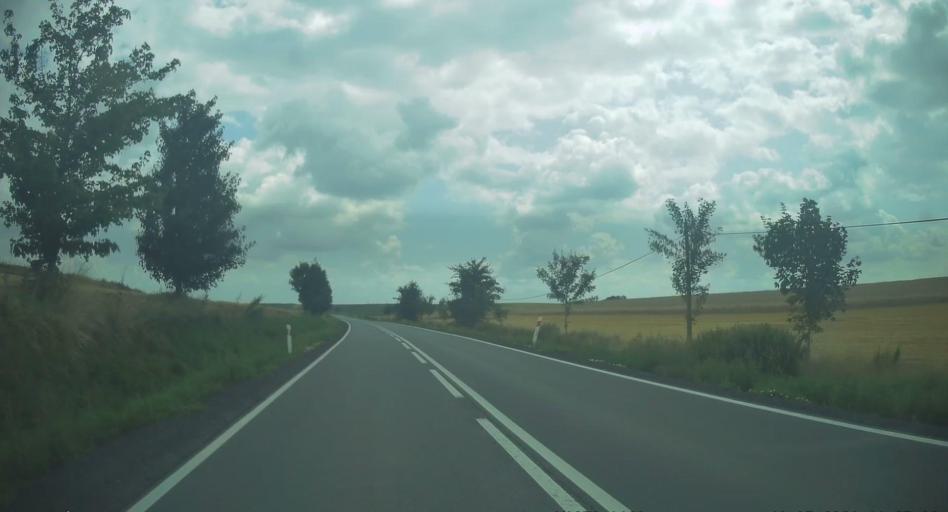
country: PL
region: Opole Voivodeship
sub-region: Powiat prudnicki
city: Raclawice Slaskie
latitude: 50.3525
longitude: 17.8052
